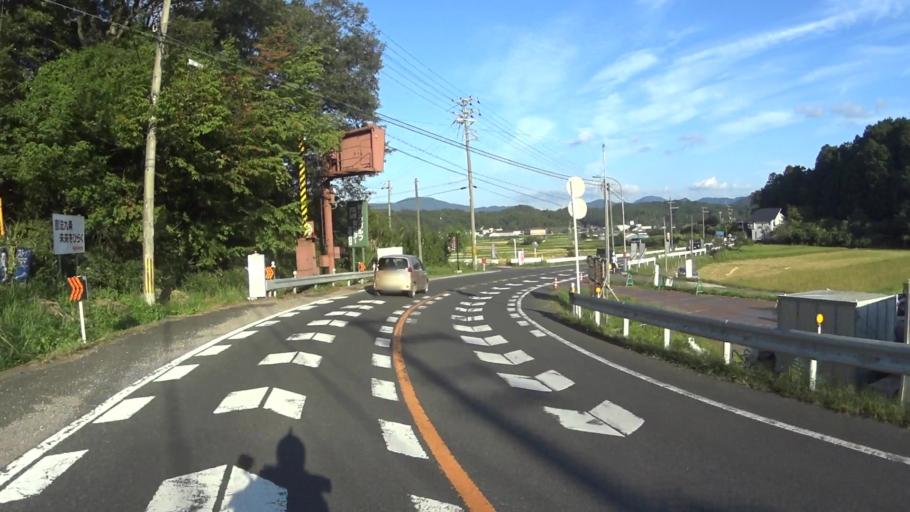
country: JP
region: Hyogo
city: Toyooka
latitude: 35.5932
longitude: 134.9198
